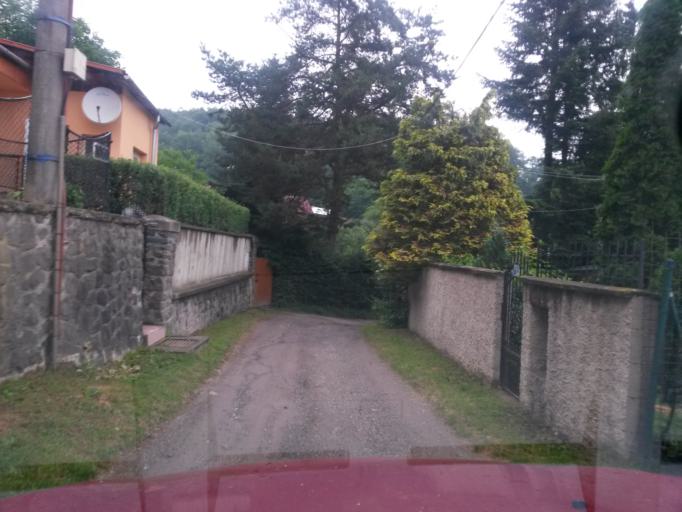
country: SK
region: Kosicky
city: Kosice
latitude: 48.7224
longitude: 21.1758
